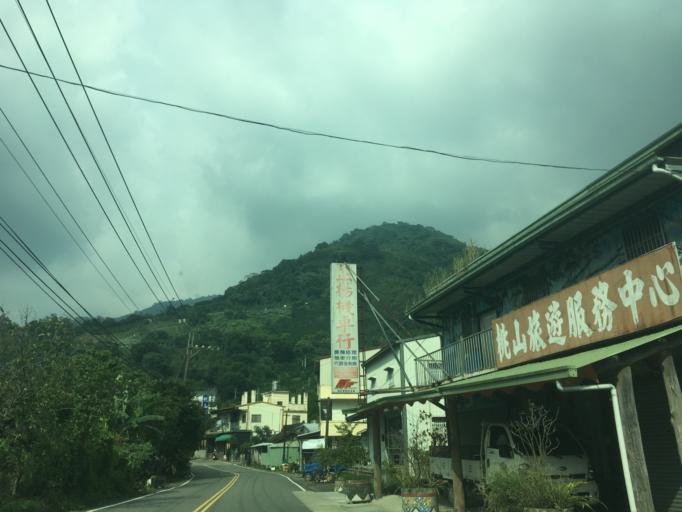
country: TW
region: Taiwan
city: Fengyuan
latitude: 24.3385
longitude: 120.9335
